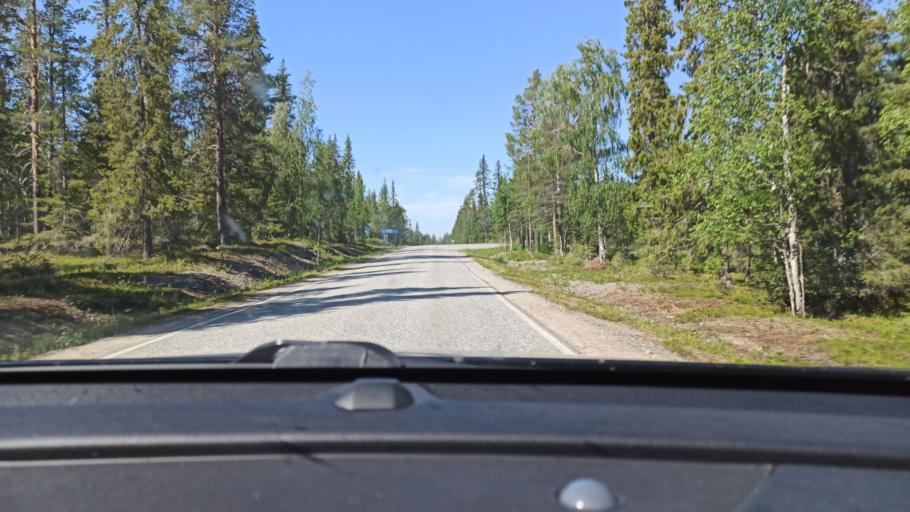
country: FI
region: Lapland
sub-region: Tunturi-Lappi
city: Kolari
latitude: 67.6841
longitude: 24.1132
